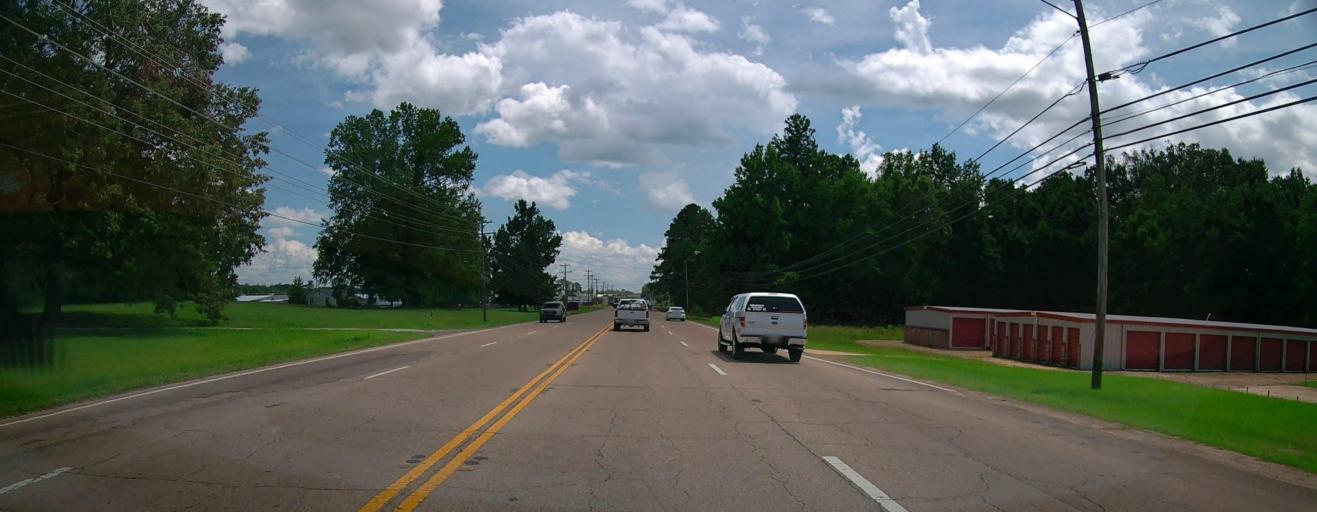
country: US
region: Mississippi
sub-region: Lee County
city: Verona
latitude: 34.1725
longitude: -88.7197
